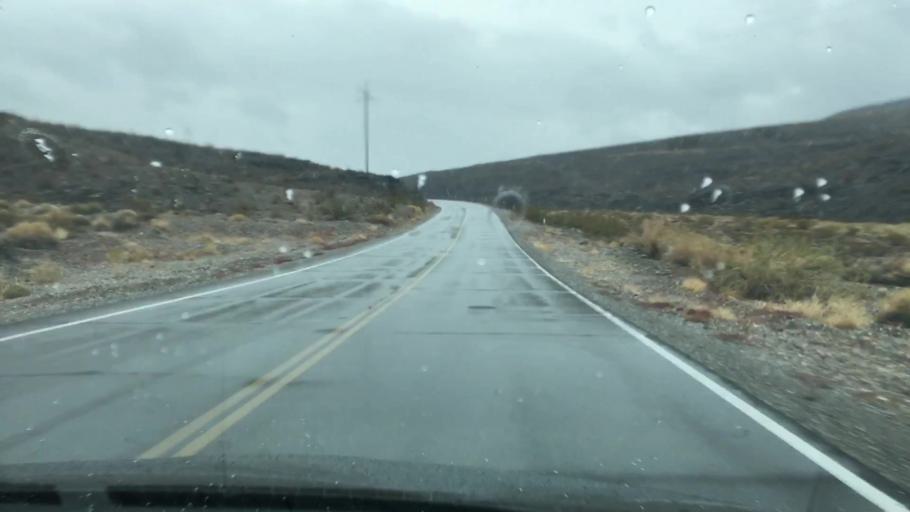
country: US
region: Nevada
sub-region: Nye County
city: Beatty
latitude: 36.3546
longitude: -116.6442
